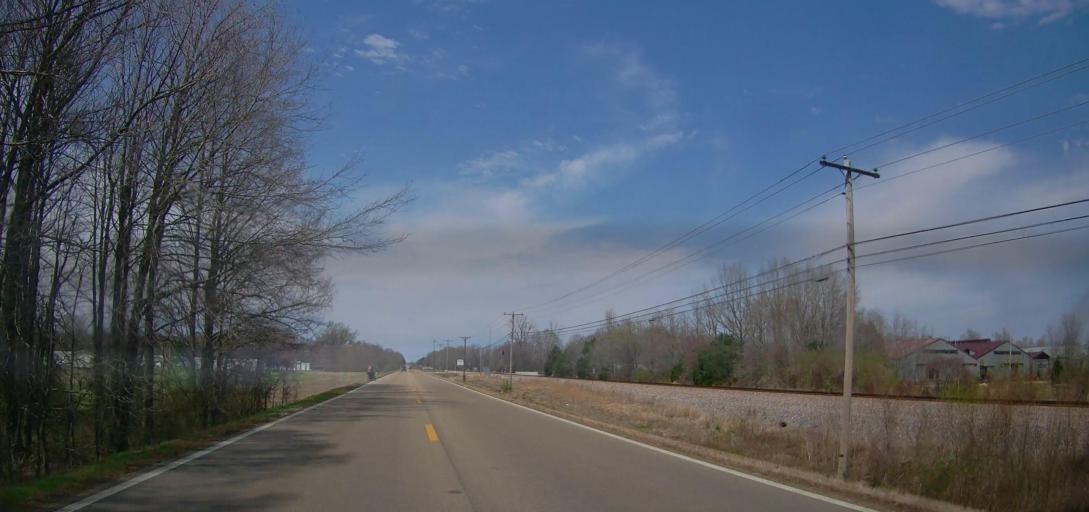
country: US
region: Mississippi
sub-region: Union County
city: New Albany
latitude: 34.5202
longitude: -89.0545
